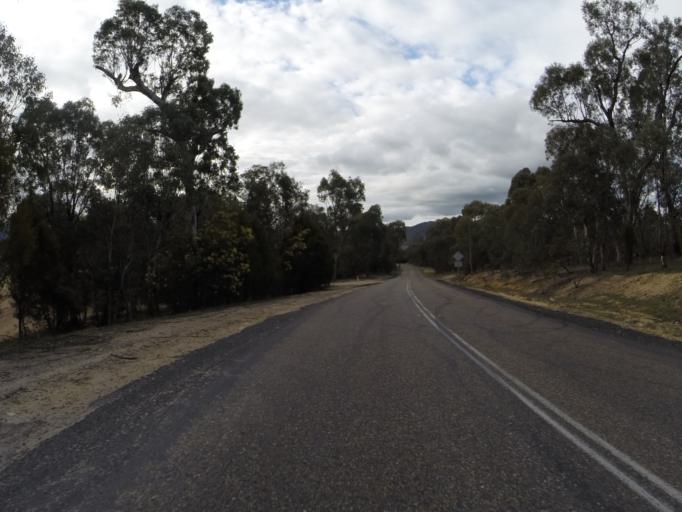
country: AU
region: Australian Capital Territory
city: Macquarie
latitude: -35.3449
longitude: 148.9293
